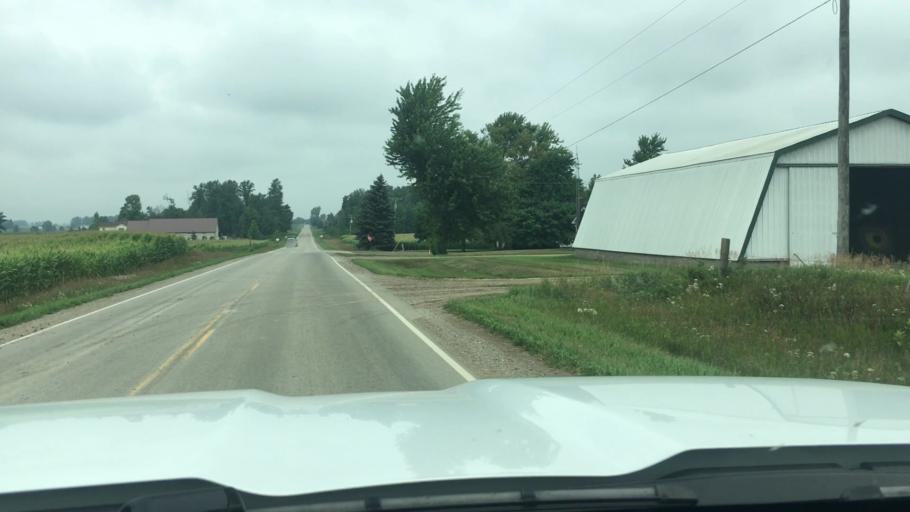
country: US
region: Michigan
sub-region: Sanilac County
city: Marlette
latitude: 43.3132
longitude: -82.9838
